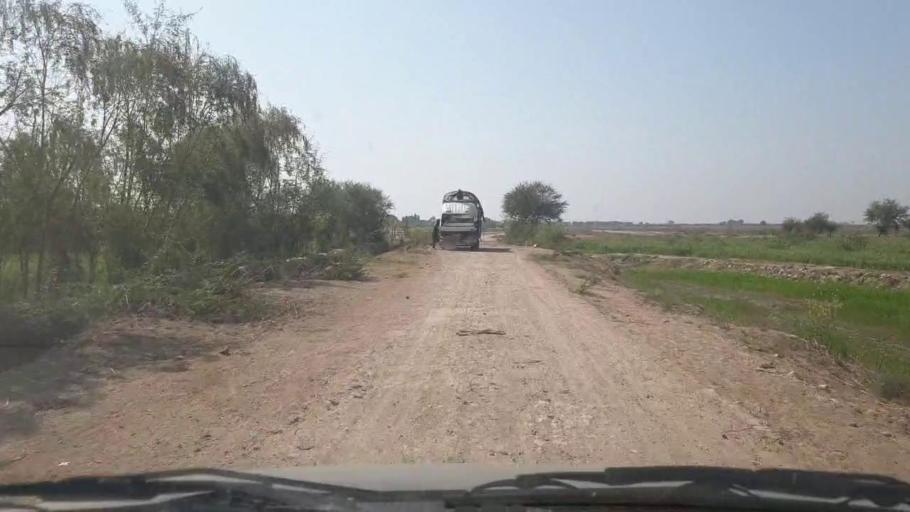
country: PK
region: Sindh
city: Samaro
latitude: 25.2672
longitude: 69.3441
